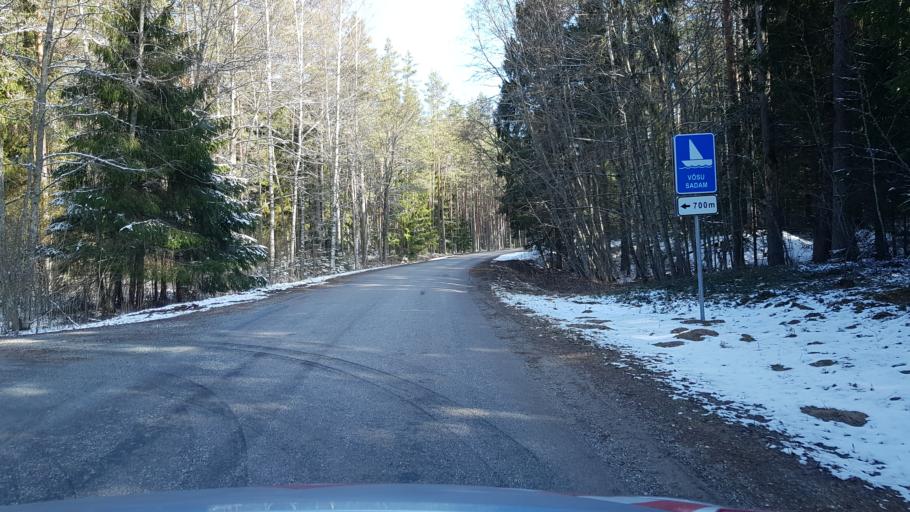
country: EE
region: Harju
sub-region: Loksa linn
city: Loksa
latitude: 59.5832
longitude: 25.9812
